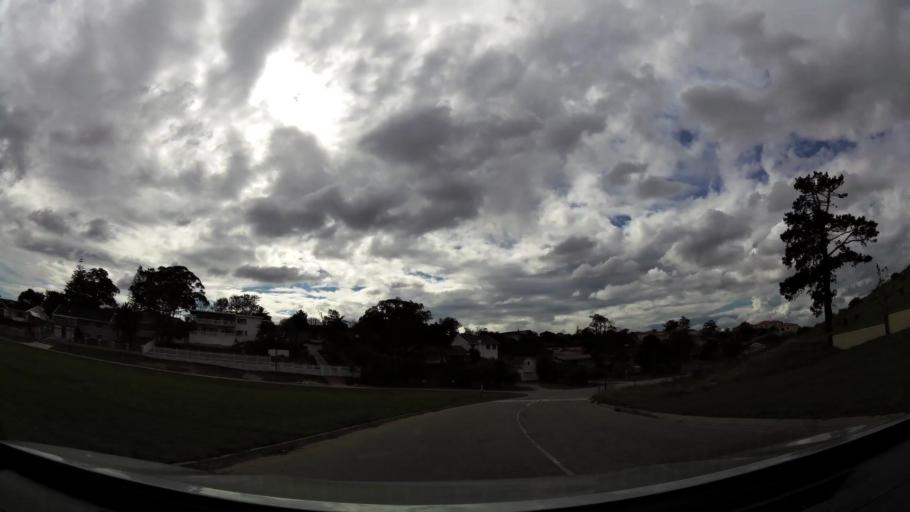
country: ZA
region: Eastern Cape
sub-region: Nelson Mandela Bay Metropolitan Municipality
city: Port Elizabeth
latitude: -33.9370
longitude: 25.5181
